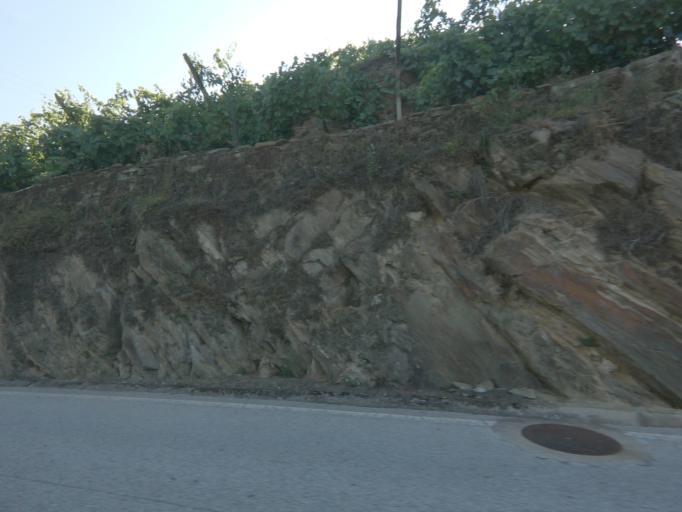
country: PT
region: Viseu
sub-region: Tabuaco
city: Tabuaco
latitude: 41.1170
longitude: -7.5628
